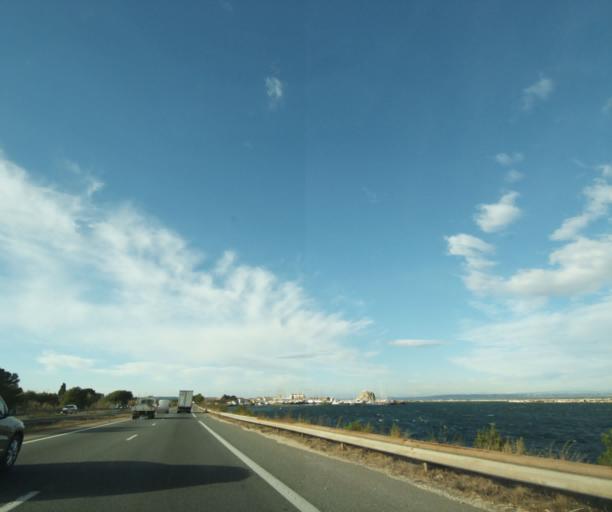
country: FR
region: Provence-Alpes-Cote d'Azur
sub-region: Departement des Bouches-du-Rhone
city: Chateauneuf-les-Martigues
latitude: 43.3983
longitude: 5.1212
